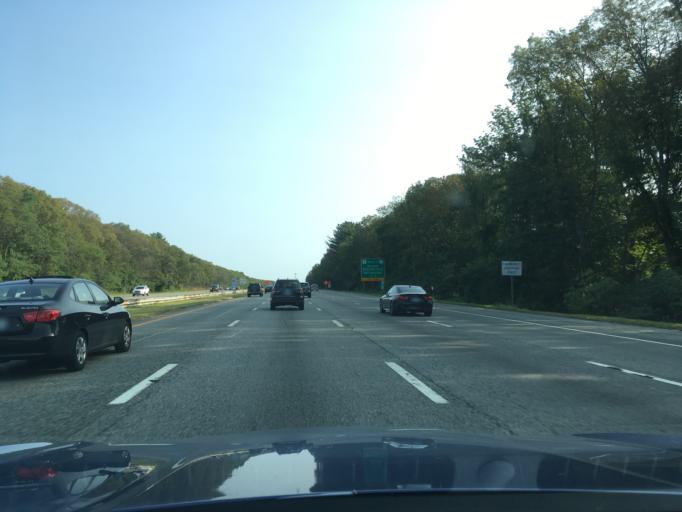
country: US
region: Rhode Island
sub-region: Kent County
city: East Greenwich
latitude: 41.6846
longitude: -71.4775
